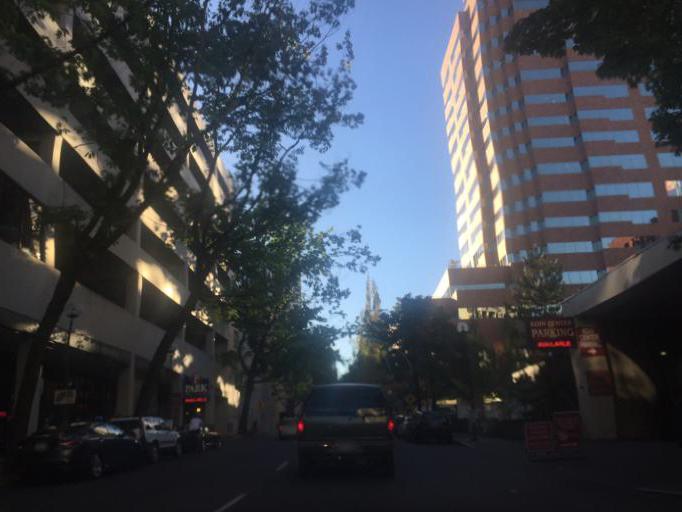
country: US
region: Oregon
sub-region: Multnomah County
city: Portland
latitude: 45.5124
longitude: -122.6764
